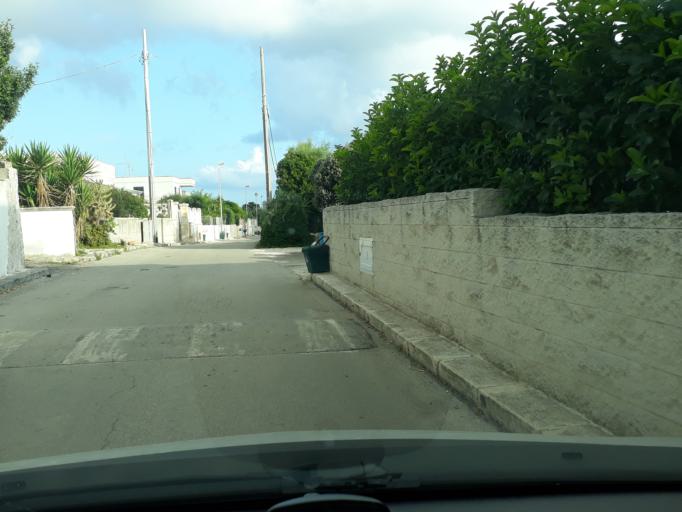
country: IT
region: Apulia
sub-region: Provincia di Brindisi
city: Carovigno
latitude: 40.7618
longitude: 17.6915
